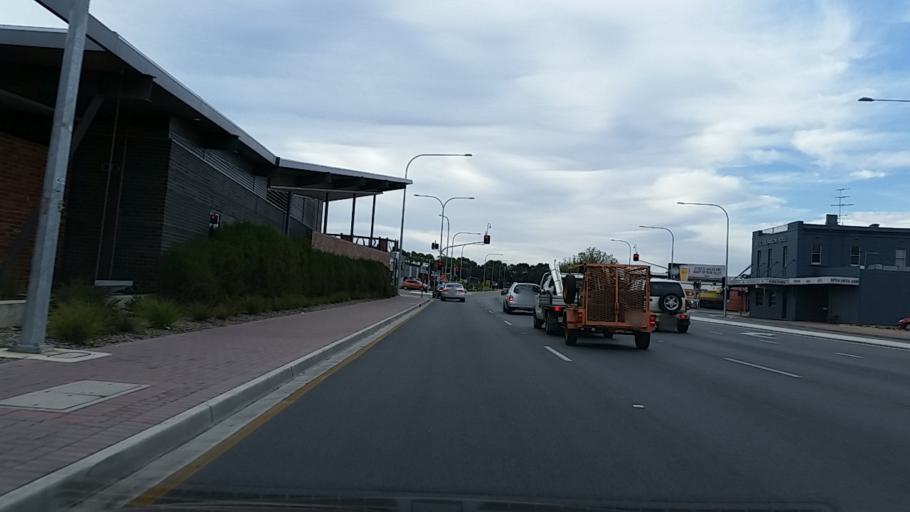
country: AU
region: South Australia
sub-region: City of West Torrens
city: Thebarton
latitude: -34.9155
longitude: 138.5663
